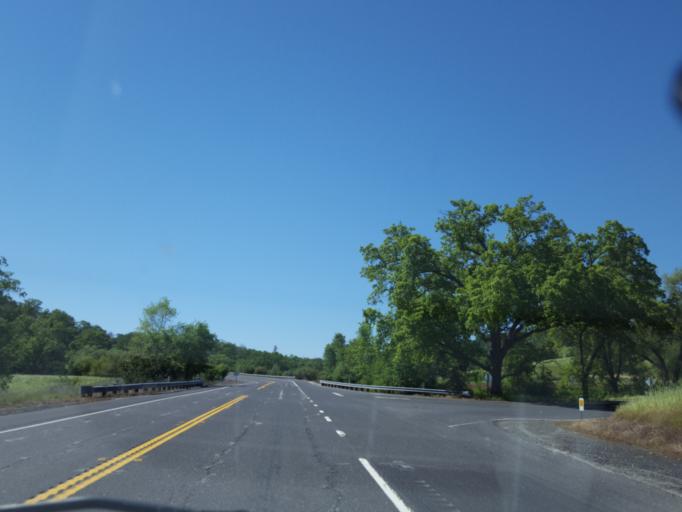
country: US
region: California
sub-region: Calaveras County
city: Angels Camp
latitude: 38.0361
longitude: -120.5090
